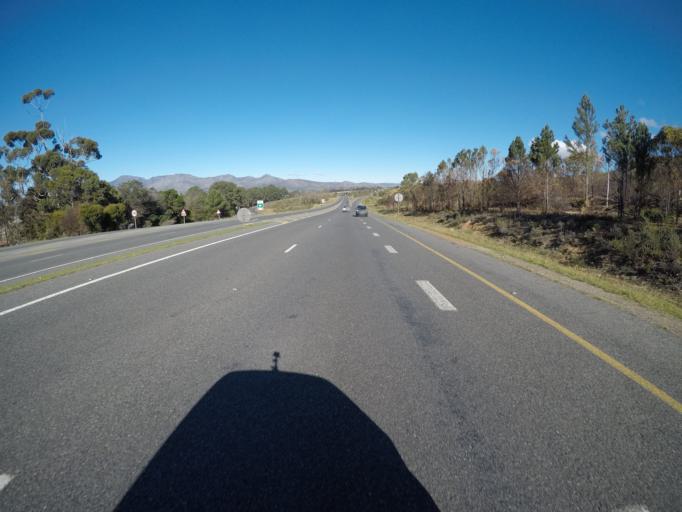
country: ZA
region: Western Cape
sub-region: Overberg District Municipality
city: Grabouw
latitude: -34.2252
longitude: 19.1877
